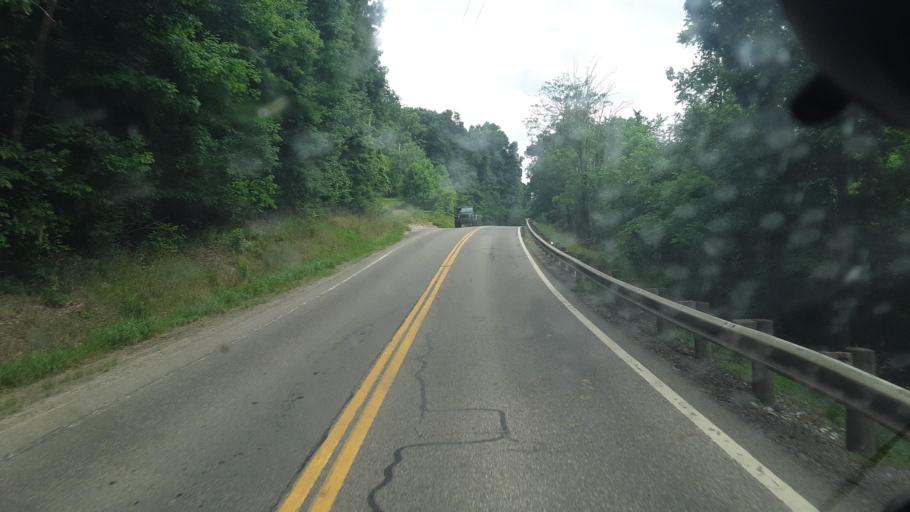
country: US
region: Ohio
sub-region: Coshocton County
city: West Lafayette
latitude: 40.3951
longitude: -81.7165
